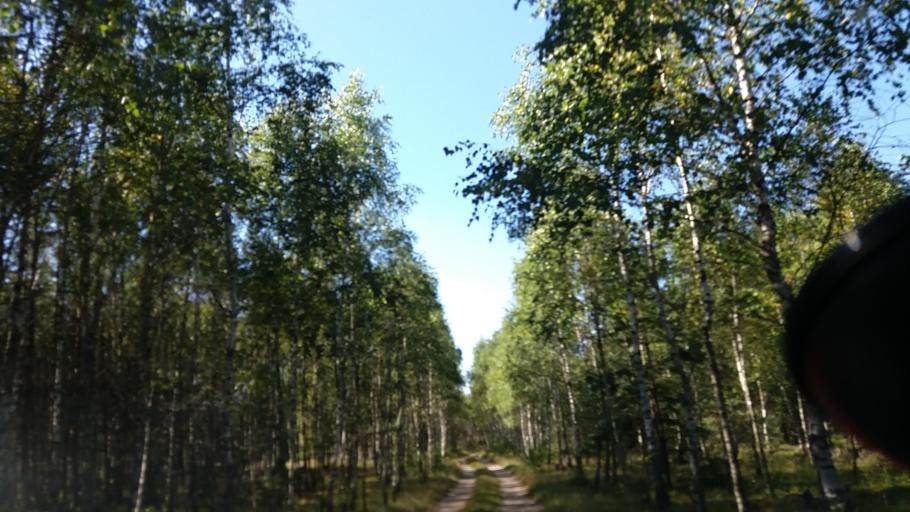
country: PL
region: West Pomeranian Voivodeship
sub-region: Powiat szczecinecki
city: Borne Sulinowo
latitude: 53.5680
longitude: 16.5326
